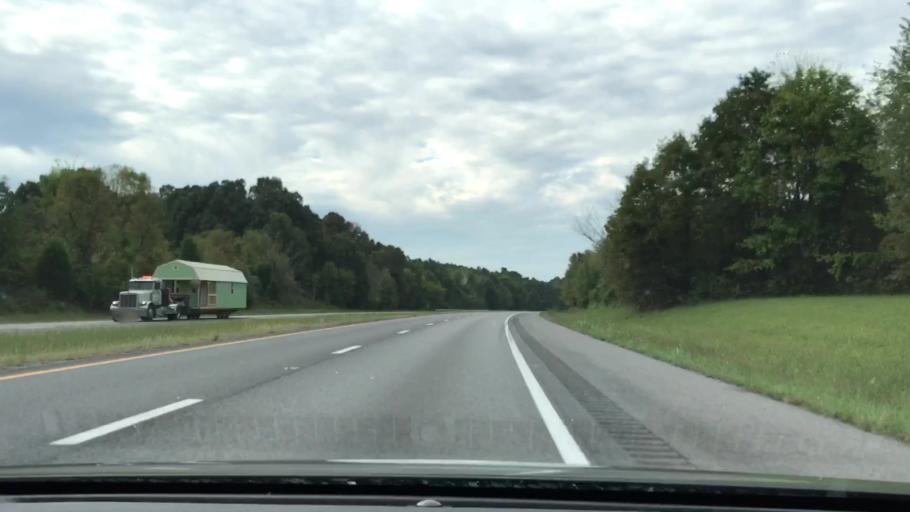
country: US
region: Kentucky
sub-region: Marshall County
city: Benton
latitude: 36.8998
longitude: -88.3476
